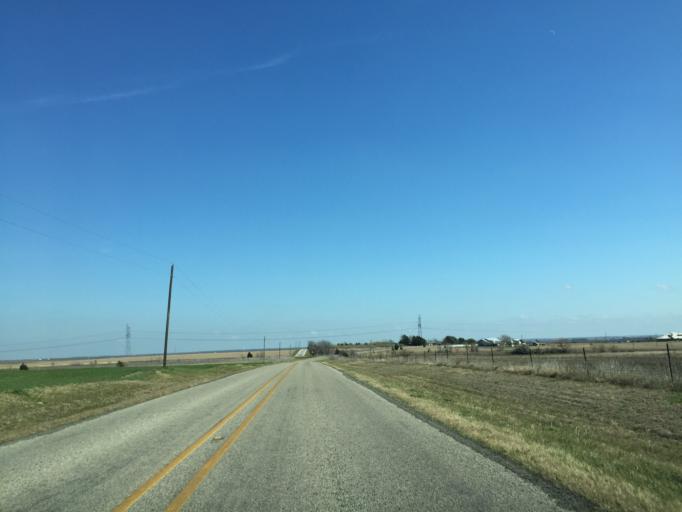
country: US
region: Texas
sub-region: Williamson County
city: Granger
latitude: 30.7577
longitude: -97.5319
